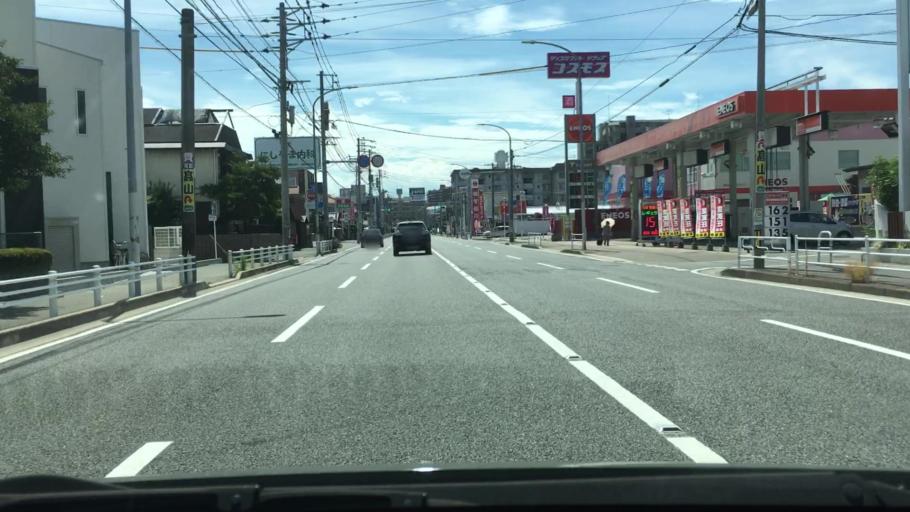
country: JP
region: Fukuoka
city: Onojo
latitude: 33.5520
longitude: 130.4570
